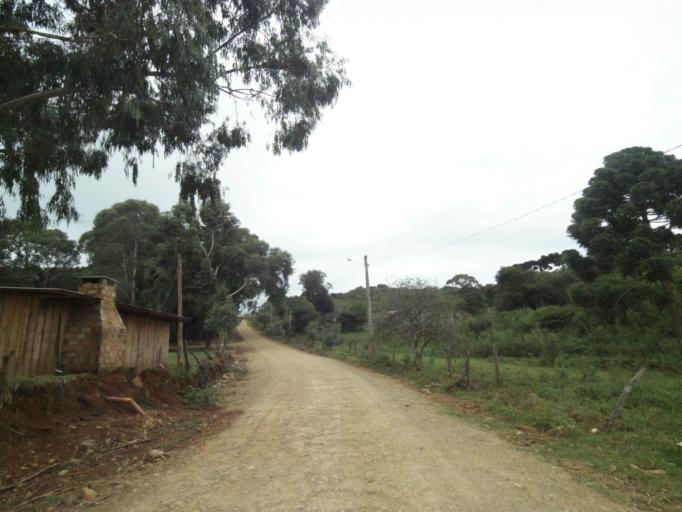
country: BR
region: Rio Grande do Sul
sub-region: Lagoa Vermelha
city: Lagoa Vermelha
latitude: -28.2004
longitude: -51.5353
